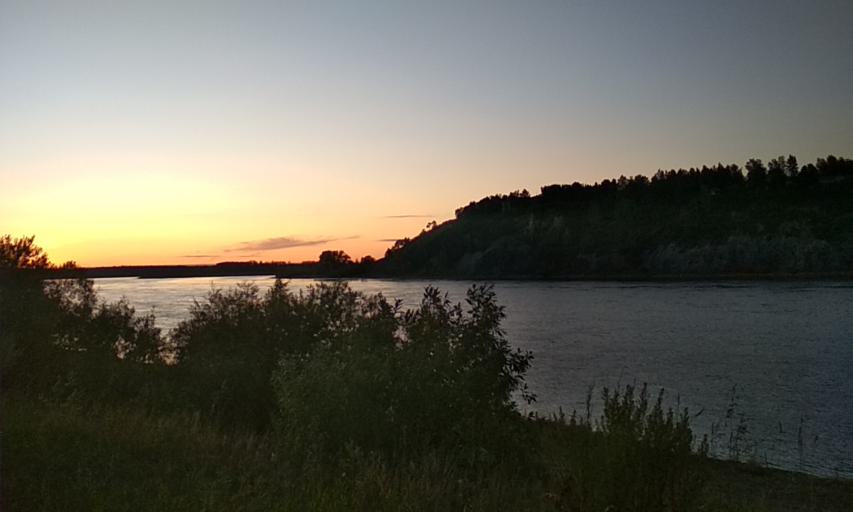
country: RU
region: Tomsk
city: Kaltay
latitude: 56.3272
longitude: 84.9226
